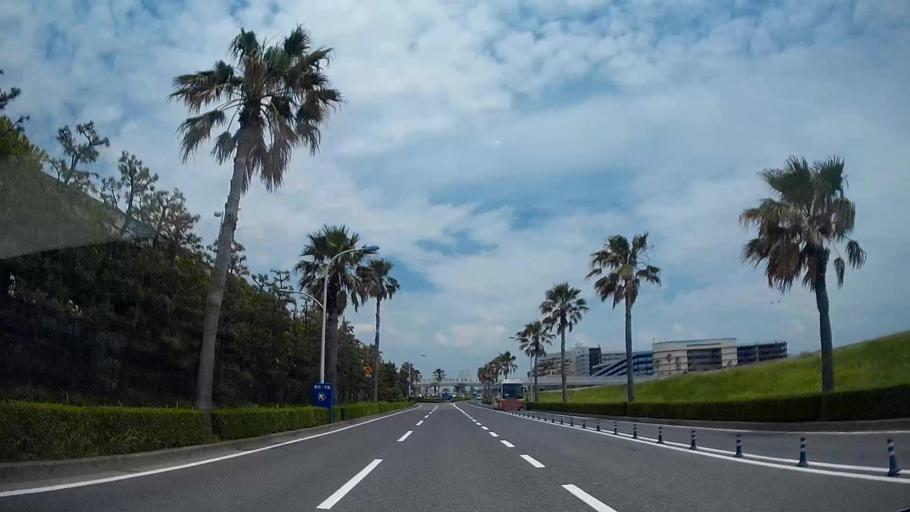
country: JP
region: Tokyo
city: Urayasu
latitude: 35.6249
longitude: 139.8910
